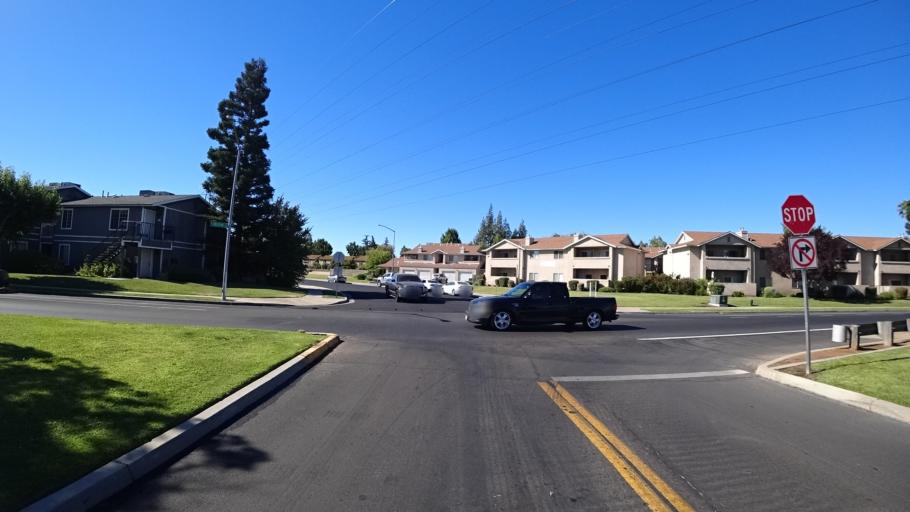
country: US
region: California
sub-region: Fresno County
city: Fresno
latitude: 36.7963
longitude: -119.8299
